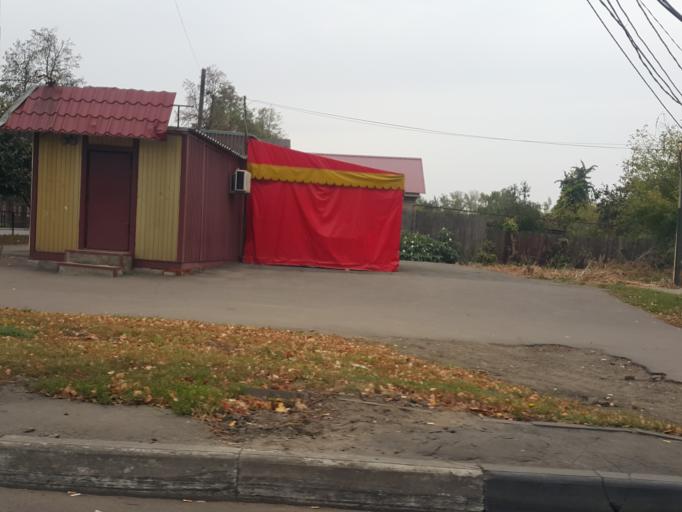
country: RU
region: Tambov
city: Tambov
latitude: 52.7114
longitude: 41.4574
